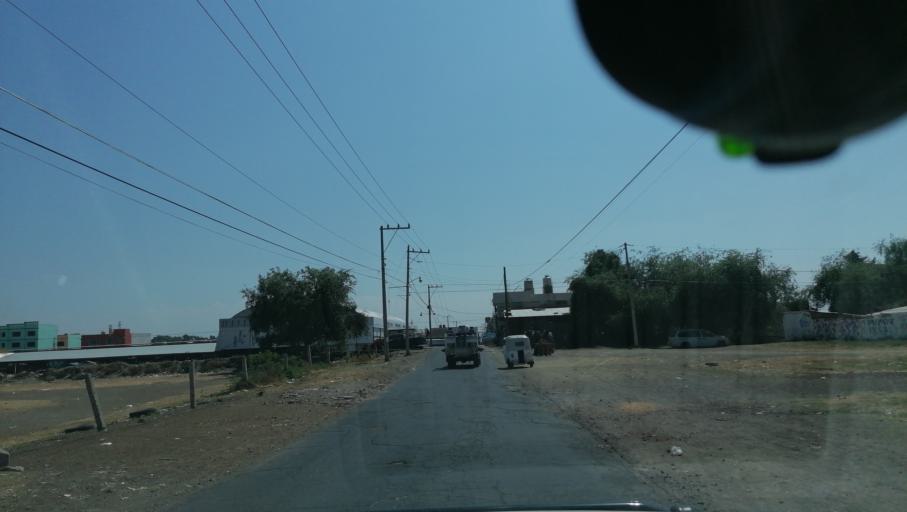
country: MX
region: Puebla
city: Huejotzingo
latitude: 19.1564
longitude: -98.4143
